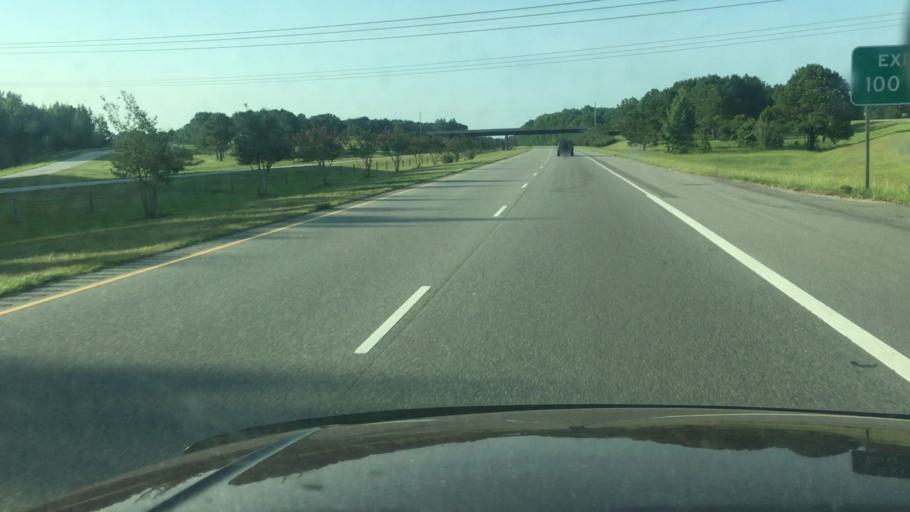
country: US
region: North Carolina
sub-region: Cumberland County
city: Fayetteville
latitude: 35.0128
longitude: -78.8700
